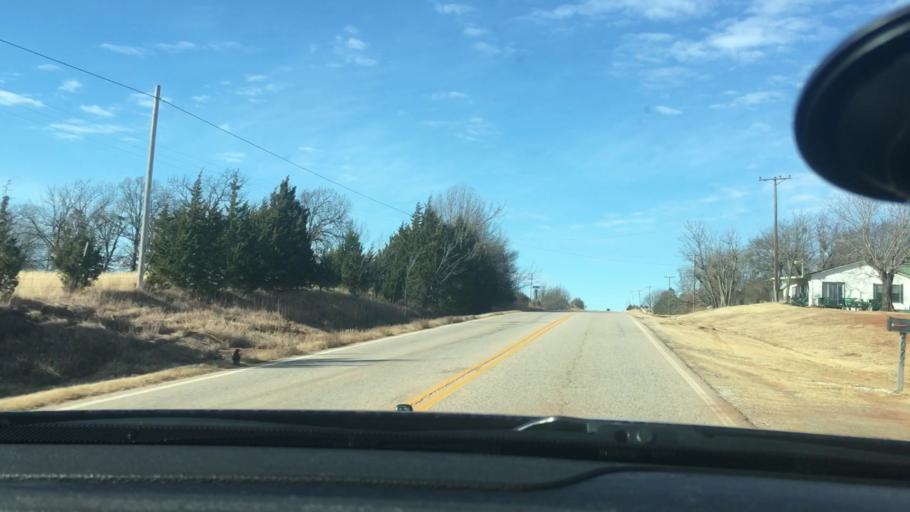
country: US
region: Oklahoma
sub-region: Seminole County
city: Konawa
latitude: 34.9860
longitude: -96.9387
